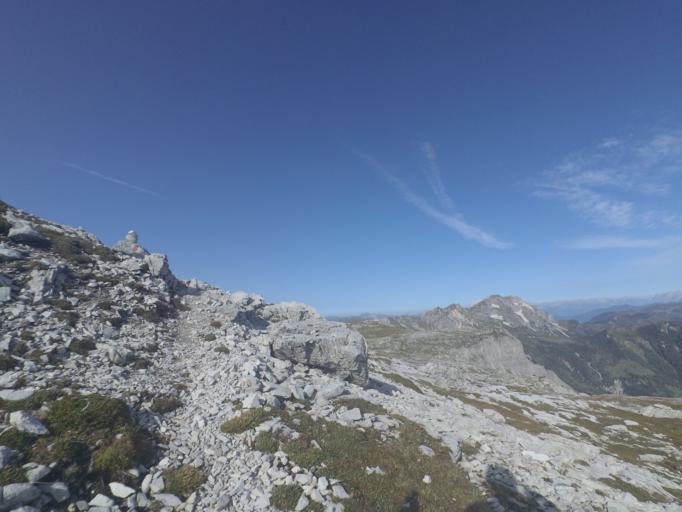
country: AT
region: Salzburg
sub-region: Politischer Bezirk Sankt Johann im Pongau
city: Kleinarl
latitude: 47.2229
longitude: 13.4067
